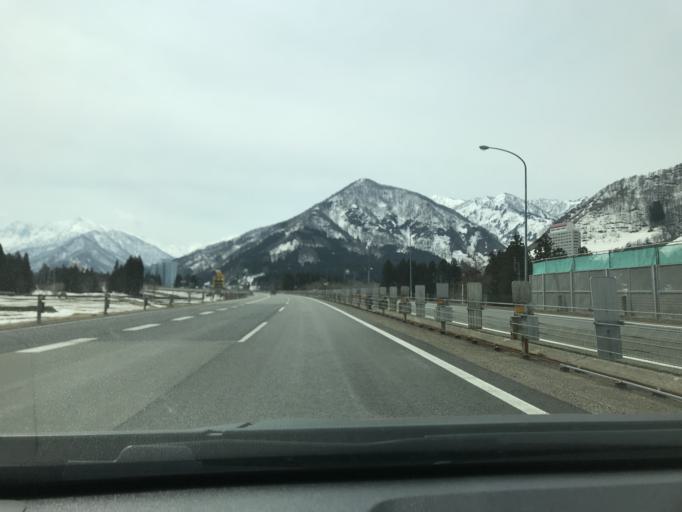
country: JP
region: Niigata
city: Shiozawa
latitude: 36.9173
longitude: 138.8418
